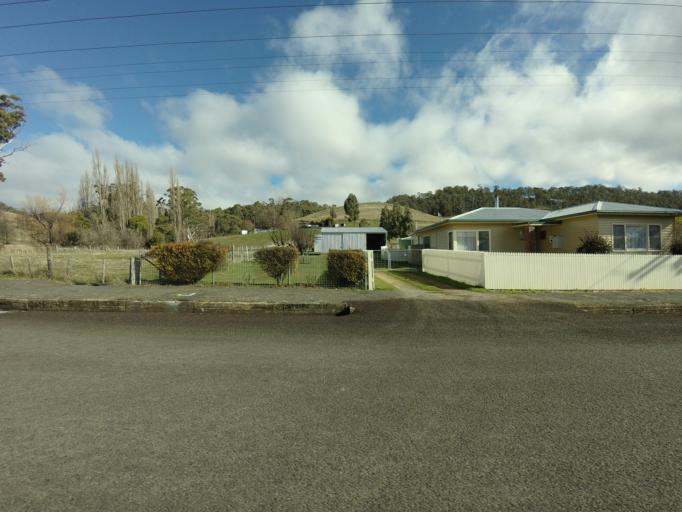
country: AU
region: Tasmania
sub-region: Derwent Valley
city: New Norfolk
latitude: -42.6150
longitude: 146.7150
